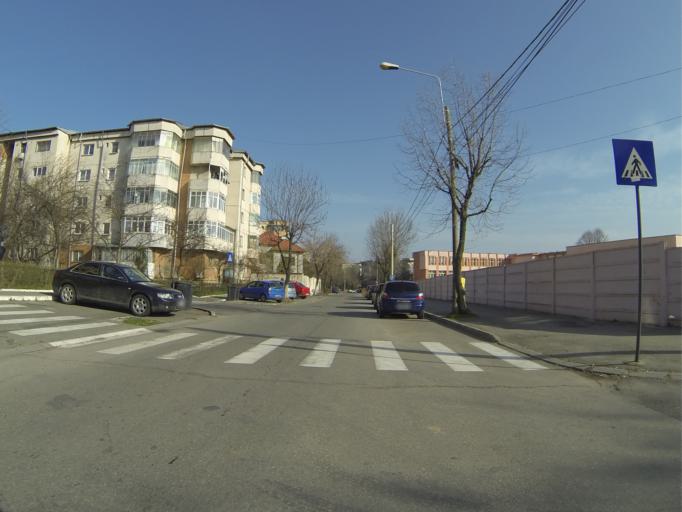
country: RO
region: Dolj
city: Craiova
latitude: 44.3256
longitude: 23.8154
